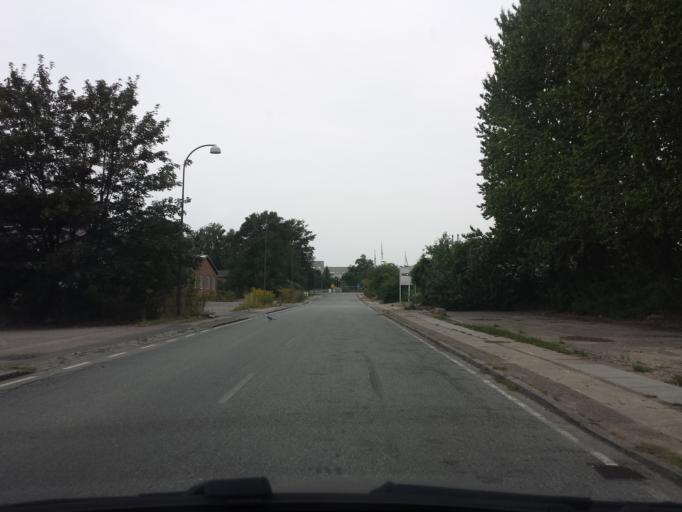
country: DK
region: Capital Region
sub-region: Herlev Kommune
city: Herlev
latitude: 55.7188
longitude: 12.4325
